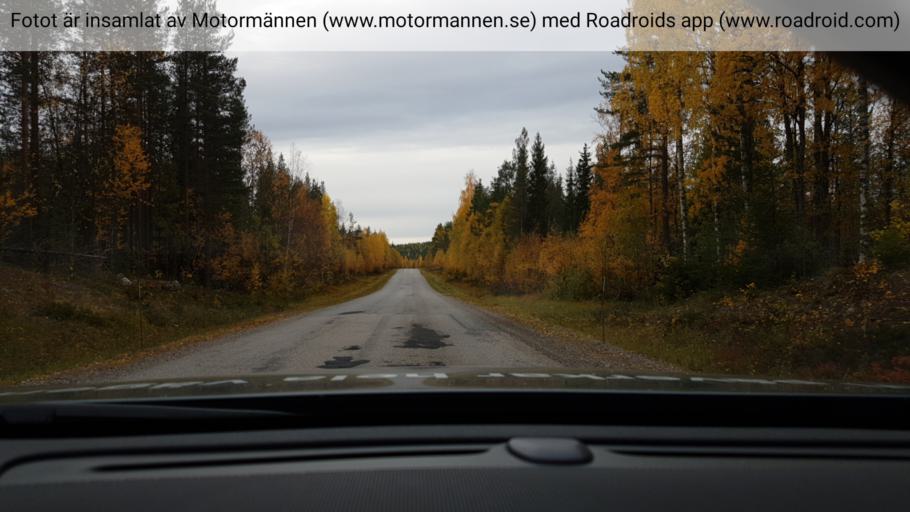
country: SE
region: Norrbotten
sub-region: Overkalix Kommun
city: OEverkalix
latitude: 66.2526
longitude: 23.0164
